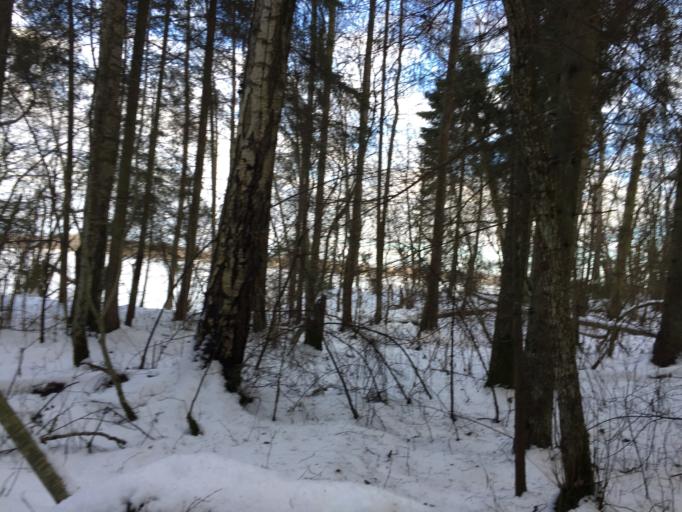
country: LV
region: Lielvarde
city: Lielvarde
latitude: 56.7057
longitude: 24.7933
